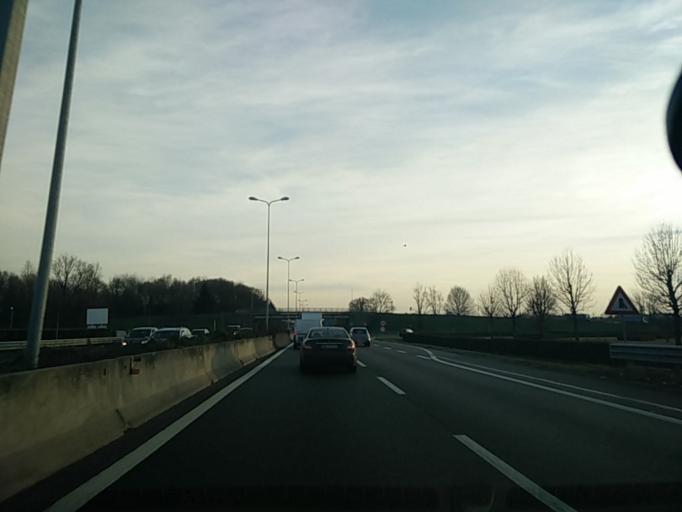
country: IT
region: Lombardy
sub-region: Citta metropolitana di Milano
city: Paderno Dugnano
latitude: 45.5806
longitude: 9.1753
